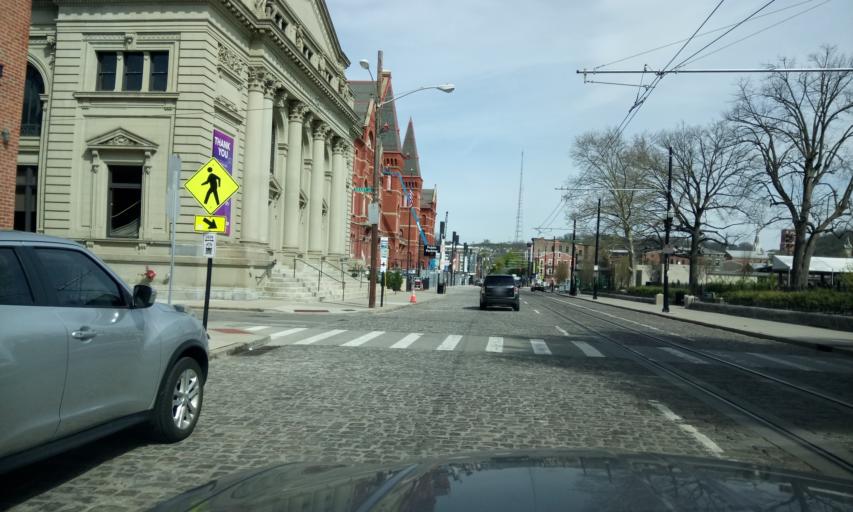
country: US
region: Kentucky
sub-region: Kenton County
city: Covington
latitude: 39.1083
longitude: -84.5181
